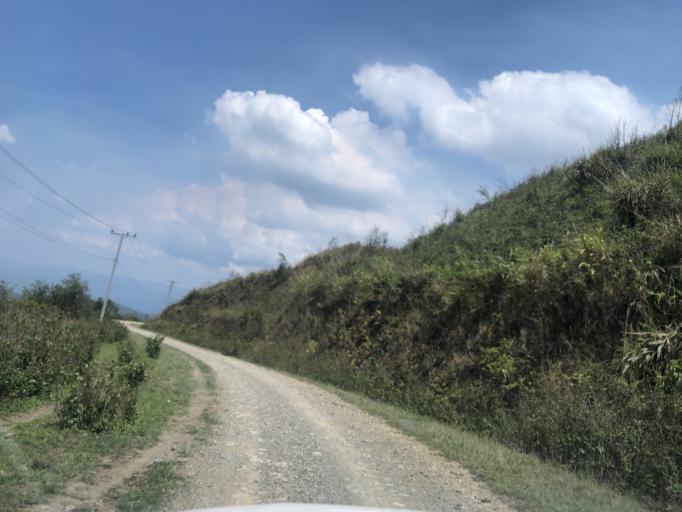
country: LA
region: Phongsali
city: Phongsali
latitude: 21.4123
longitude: 102.1869
